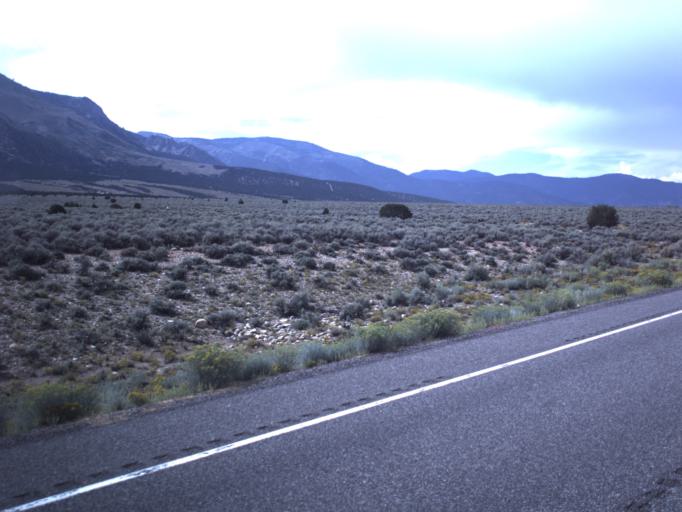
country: US
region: Utah
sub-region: Piute County
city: Junction
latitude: 38.3712
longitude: -112.2256
